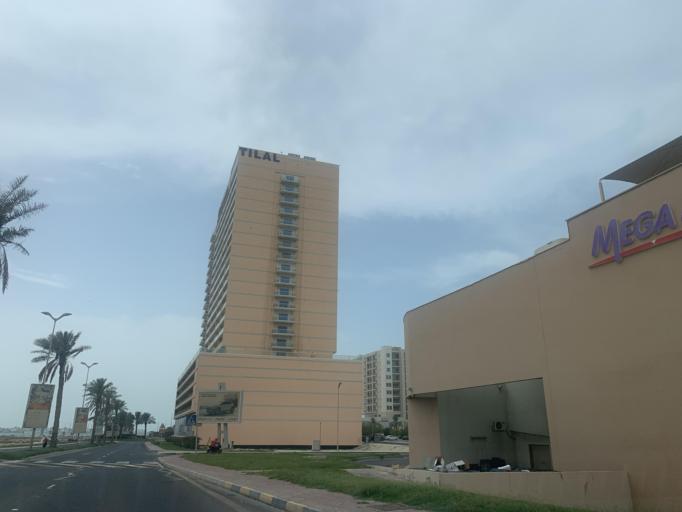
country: BH
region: Muharraq
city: Al Hadd
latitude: 26.2862
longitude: 50.6619
